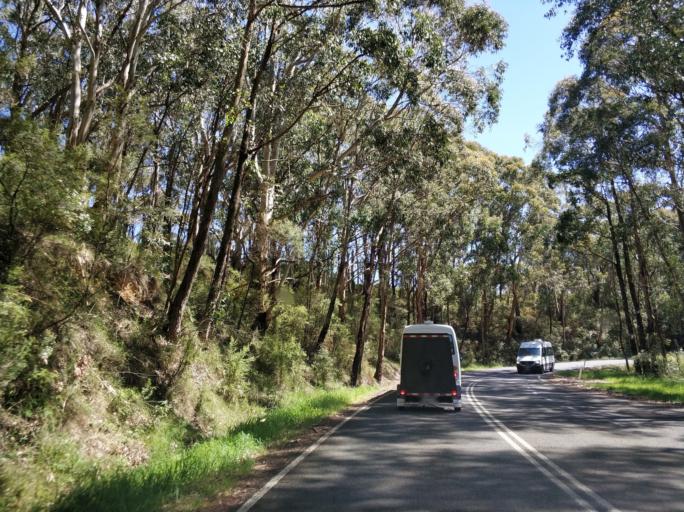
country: AU
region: Victoria
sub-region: Colac-Otway
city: Apollo Bay
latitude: -38.7474
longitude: 143.2766
